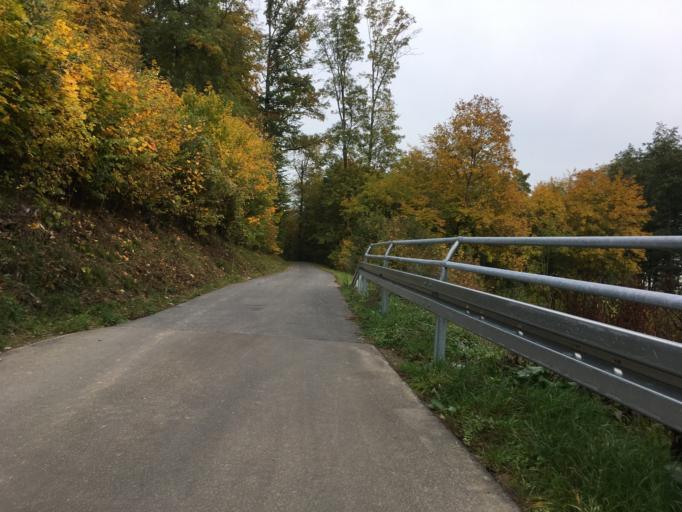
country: DE
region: Baden-Wuerttemberg
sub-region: Karlsruhe Region
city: Adelsheim
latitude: 49.4156
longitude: 9.3883
